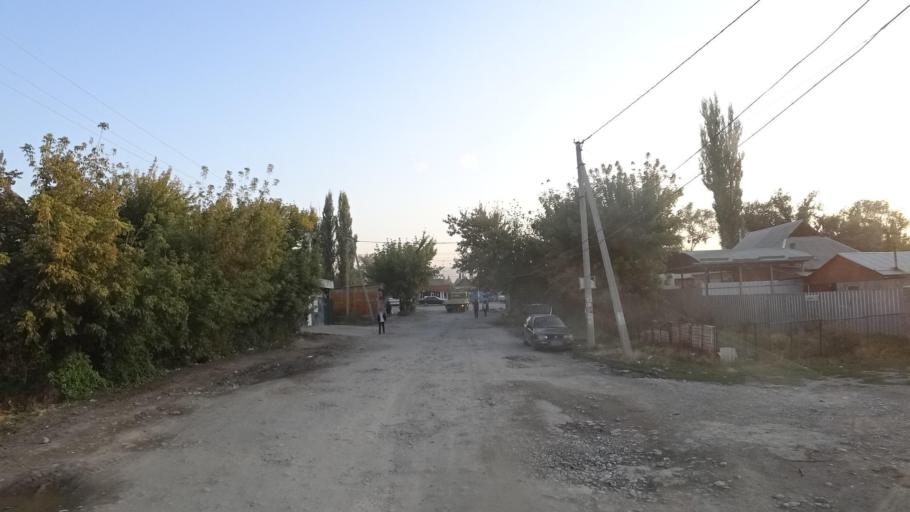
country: KG
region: Chuy
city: Lebedinovka
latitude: 42.8754
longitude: 74.7187
